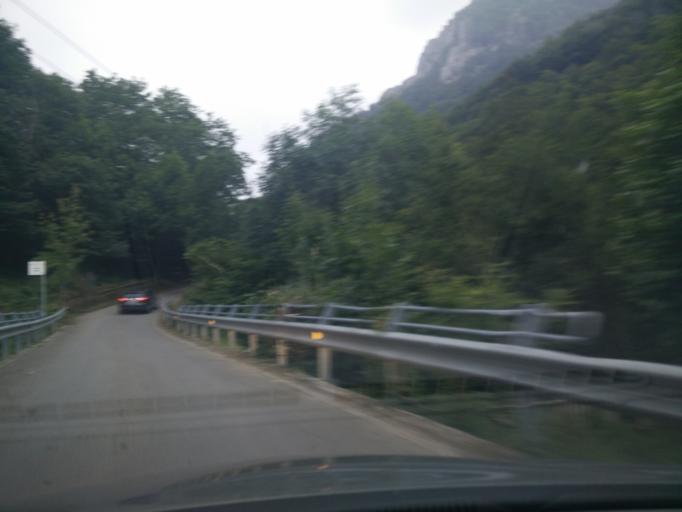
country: ES
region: Asturias
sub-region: Province of Asturias
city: Campo de Caso
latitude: 43.1697
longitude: -5.3928
